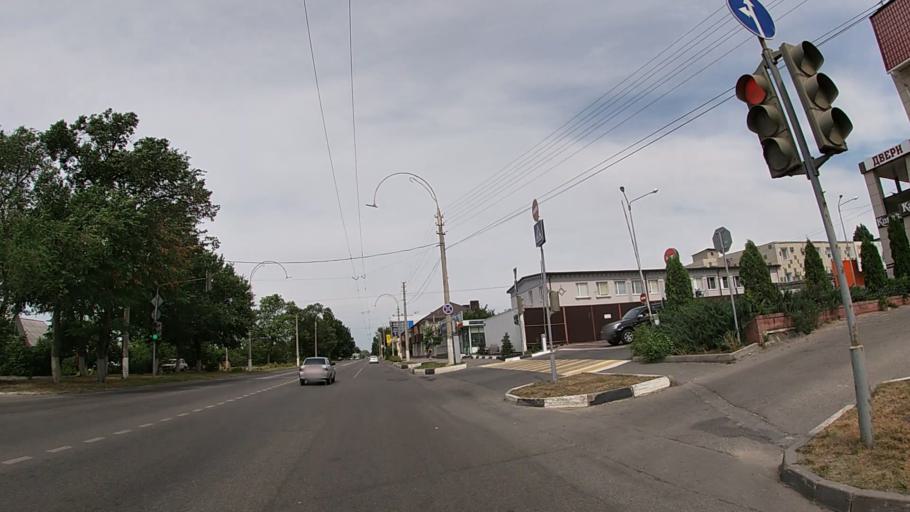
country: RU
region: Belgorod
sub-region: Belgorodskiy Rayon
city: Belgorod
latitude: 50.6033
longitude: 36.5596
